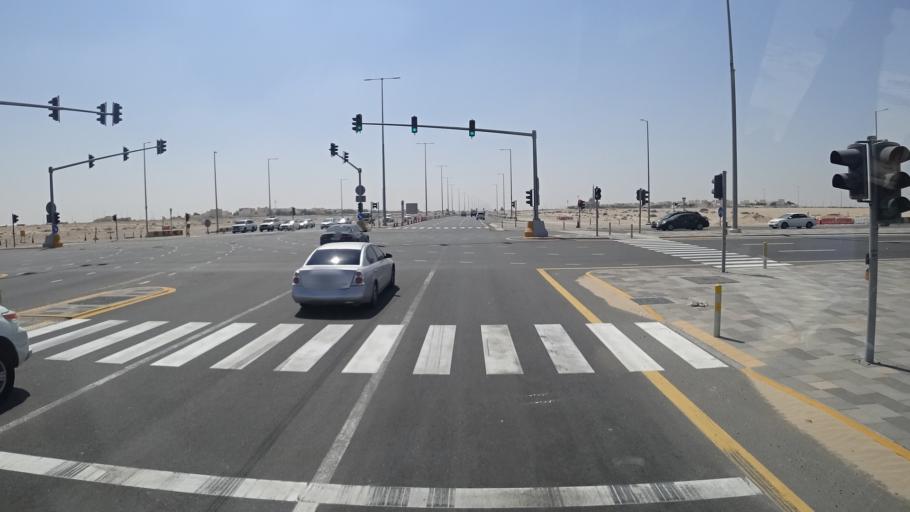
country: AE
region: Abu Dhabi
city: Abu Dhabi
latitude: 24.3377
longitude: 54.6994
